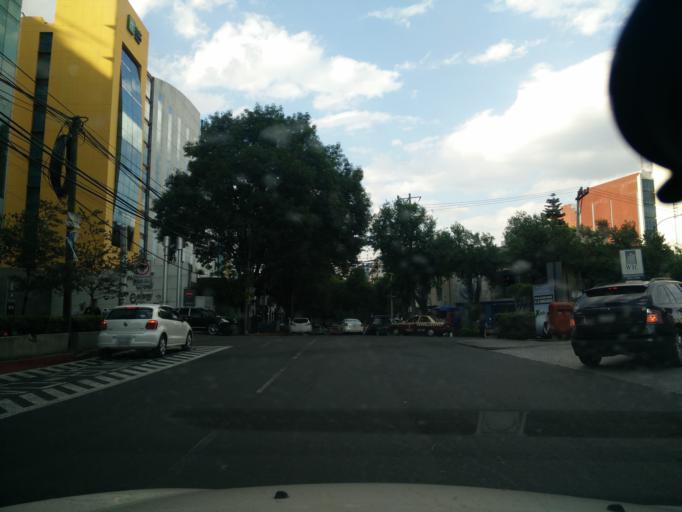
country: MX
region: Mexico City
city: Colonia del Valle
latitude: 19.3950
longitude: -99.1749
